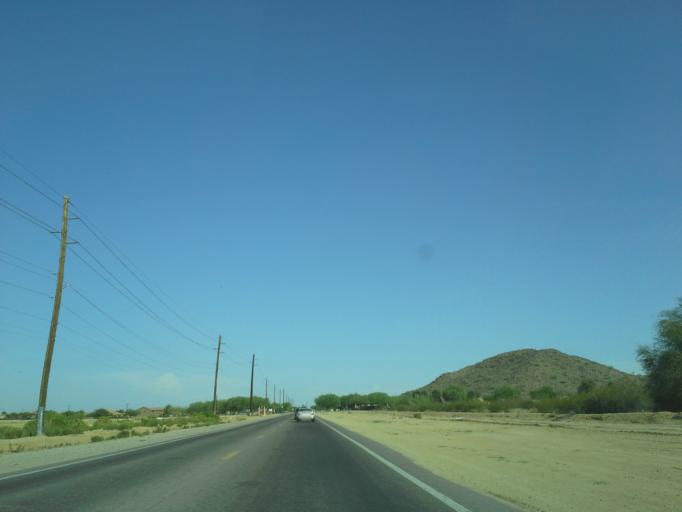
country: US
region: Arizona
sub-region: Pinal County
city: San Tan Valley
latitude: 33.1746
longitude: -111.5778
